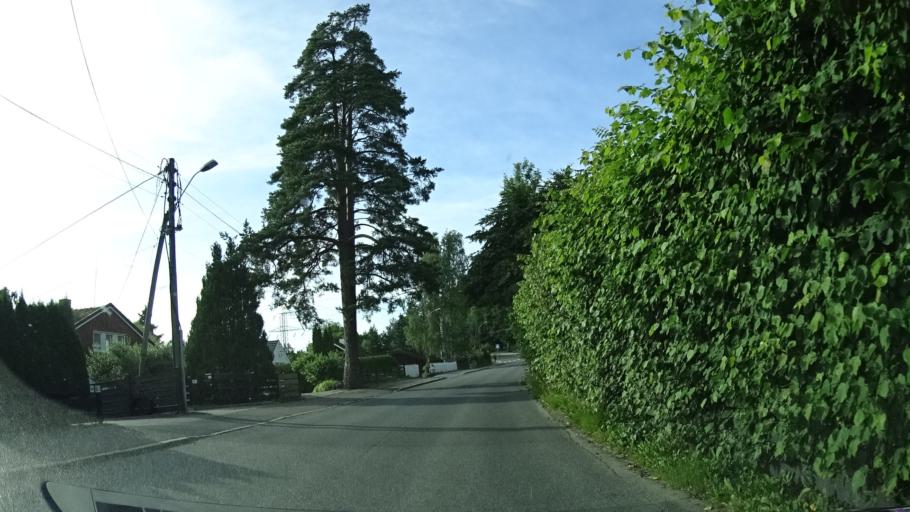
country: NO
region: Oslo
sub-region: Oslo
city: Sjolyststranda
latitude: 59.9614
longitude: 10.6476
